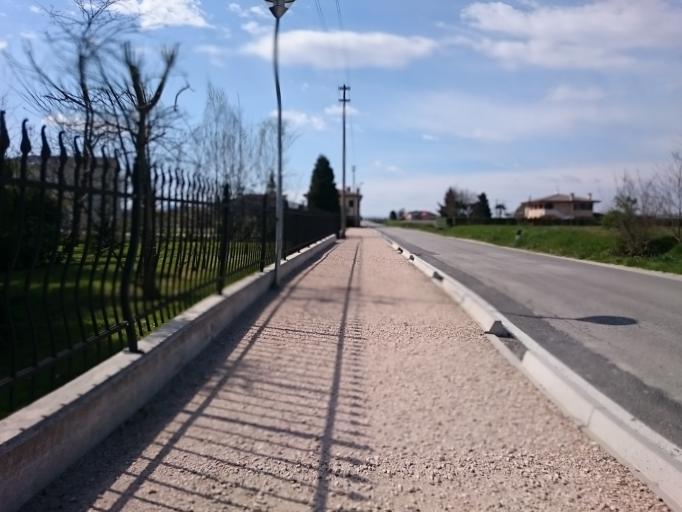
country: IT
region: Veneto
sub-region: Provincia di Padova
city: Polverara
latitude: 45.3171
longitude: 11.9590
